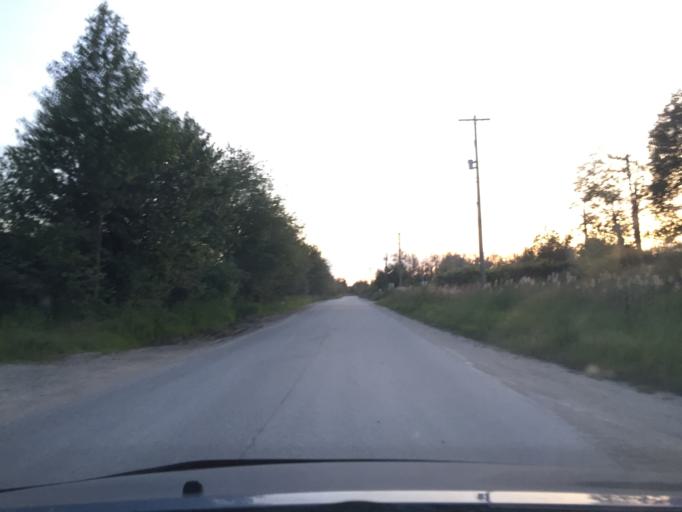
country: CA
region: British Columbia
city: Ladner
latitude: 49.1407
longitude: -123.0557
